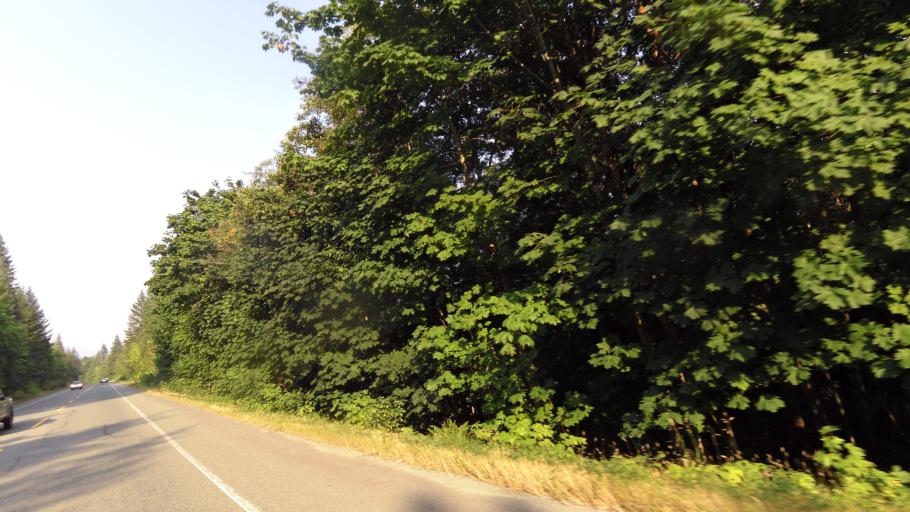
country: CA
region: British Columbia
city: Port Alberni
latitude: 49.2892
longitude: -124.9617
